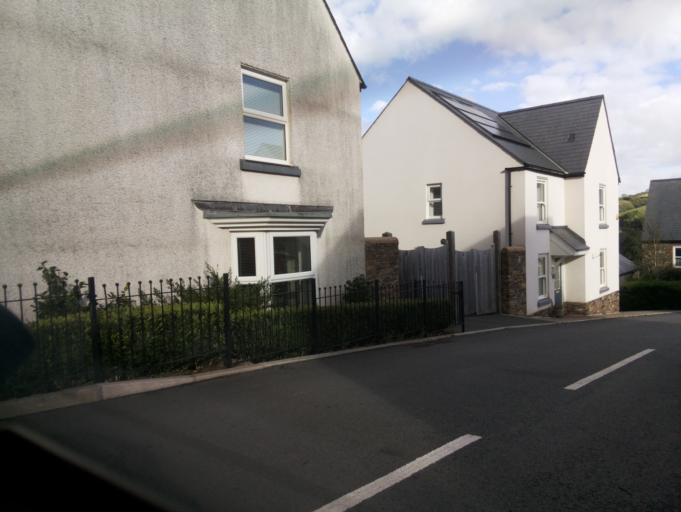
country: GB
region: England
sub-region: Devon
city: Ivybridge
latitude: 50.3640
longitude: -3.9135
